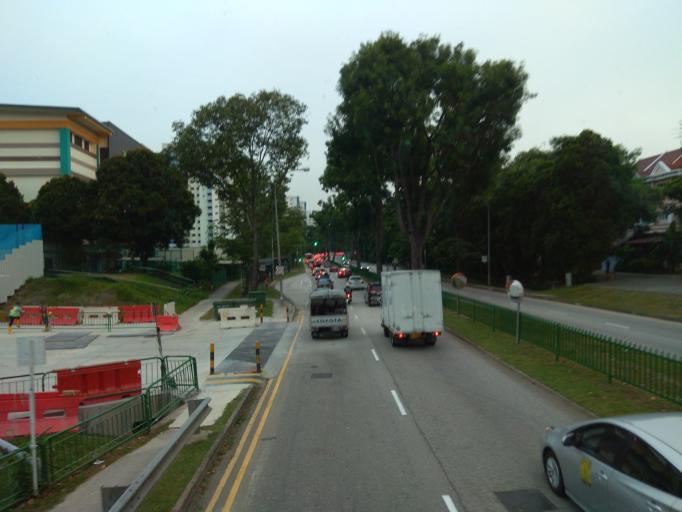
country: MY
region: Johor
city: Johor Bahru
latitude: 1.3535
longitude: 103.7002
